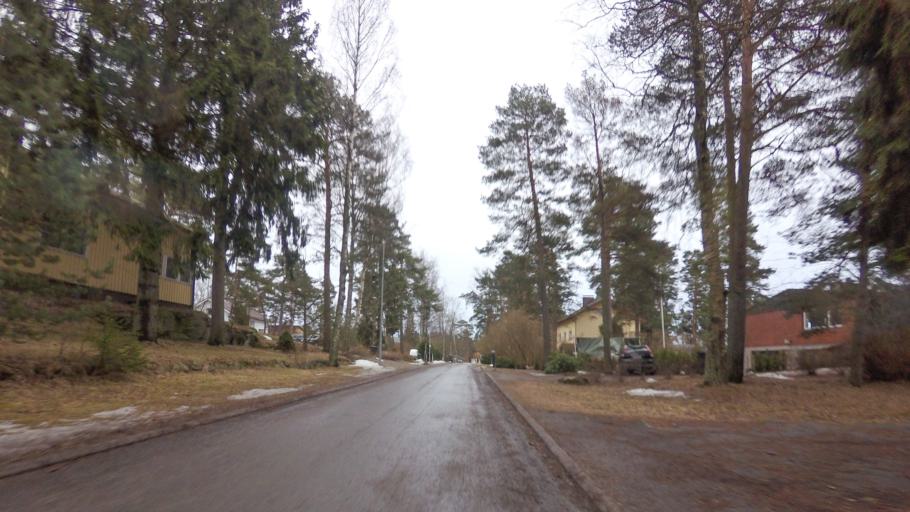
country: FI
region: Uusimaa
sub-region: Helsinki
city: Helsinki
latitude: 60.1642
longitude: 25.0531
